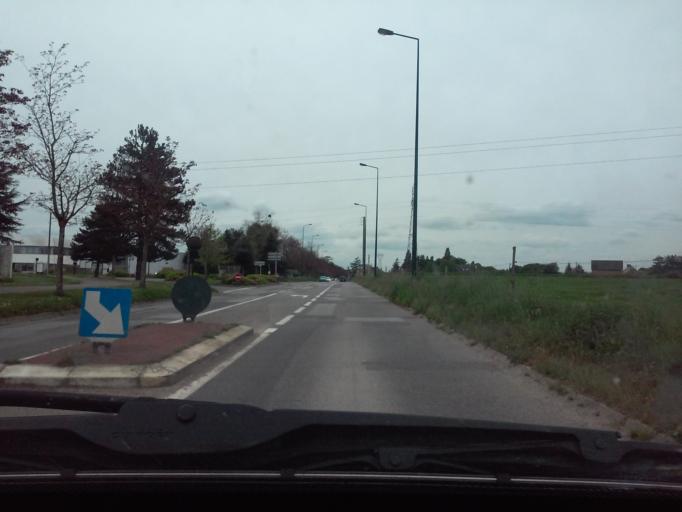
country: FR
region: Brittany
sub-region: Departement d'Ille-et-Vilaine
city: Le Rheu
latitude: 48.0971
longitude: -1.7772
